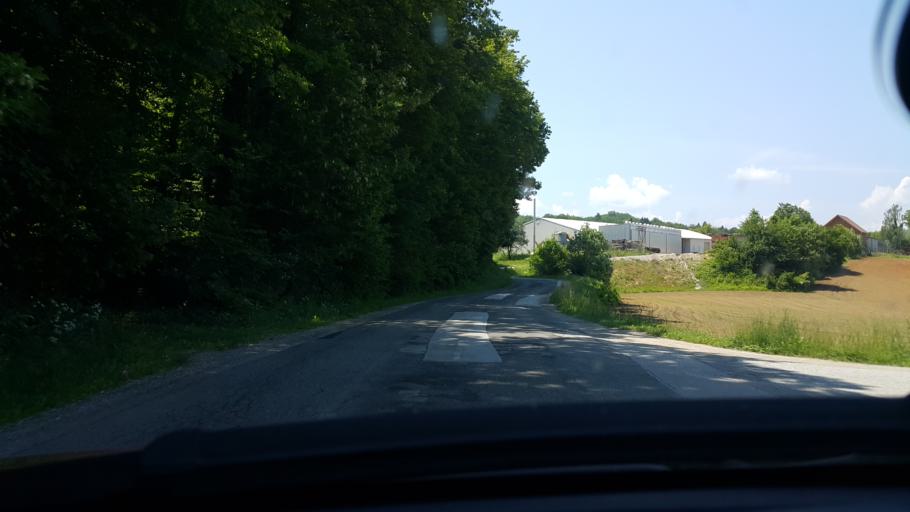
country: SI
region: Novo Mesto
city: Novo Mesto
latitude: 45.7641
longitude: 15.1581
